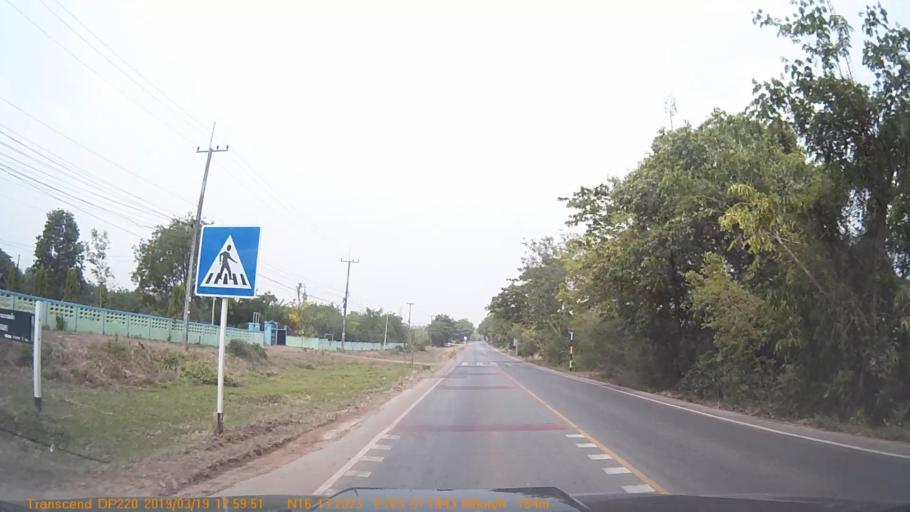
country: TH
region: Roi Et
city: Waeng
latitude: 16.2204
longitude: 103.9532
